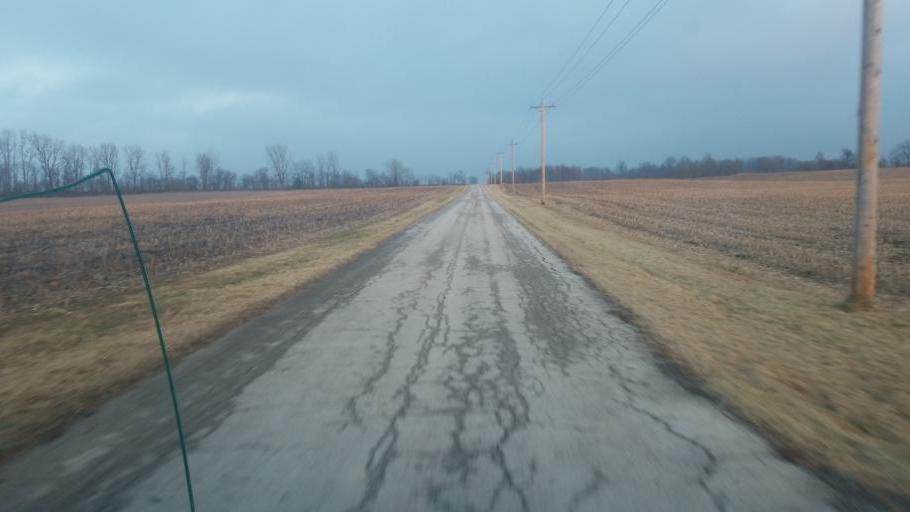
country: US
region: Ohio
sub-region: Wyandot County
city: Carey
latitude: 41.0072
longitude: -83.2725
